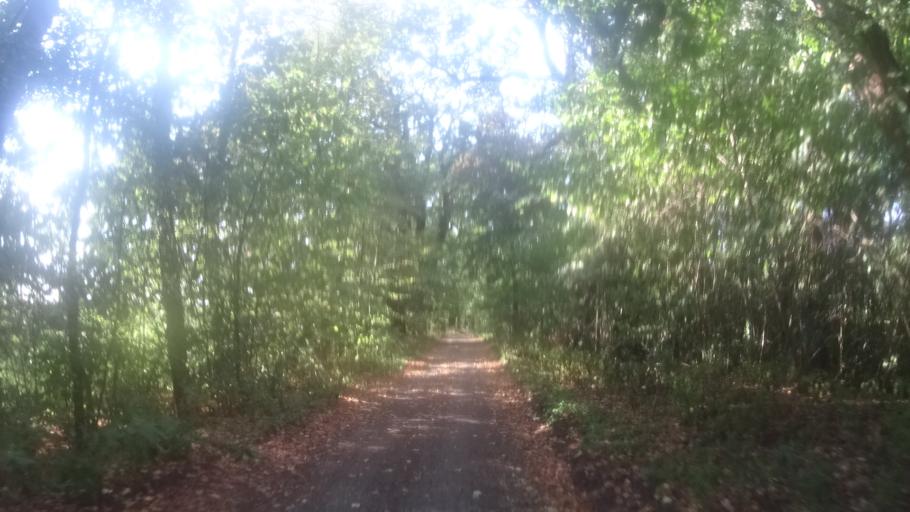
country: CZ
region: Kralovehradecky
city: Trebechovice pod Orebem
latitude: 50.1885
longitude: 16.0086
